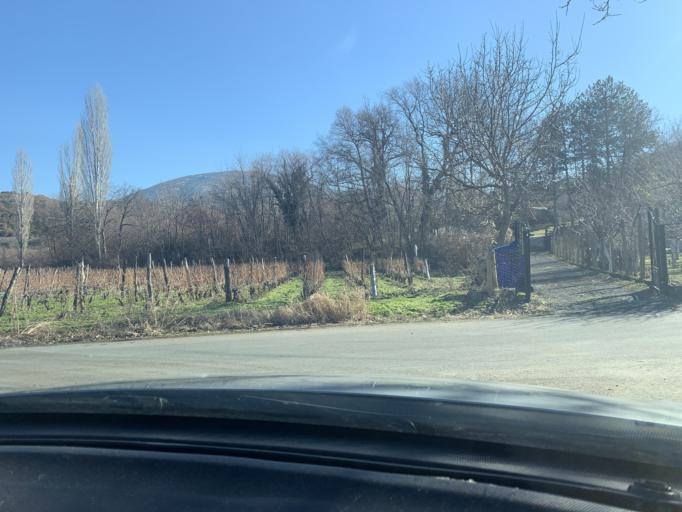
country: MK
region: Demir Kapija
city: Demir Kapija
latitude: 41.3896
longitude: 22.2257
